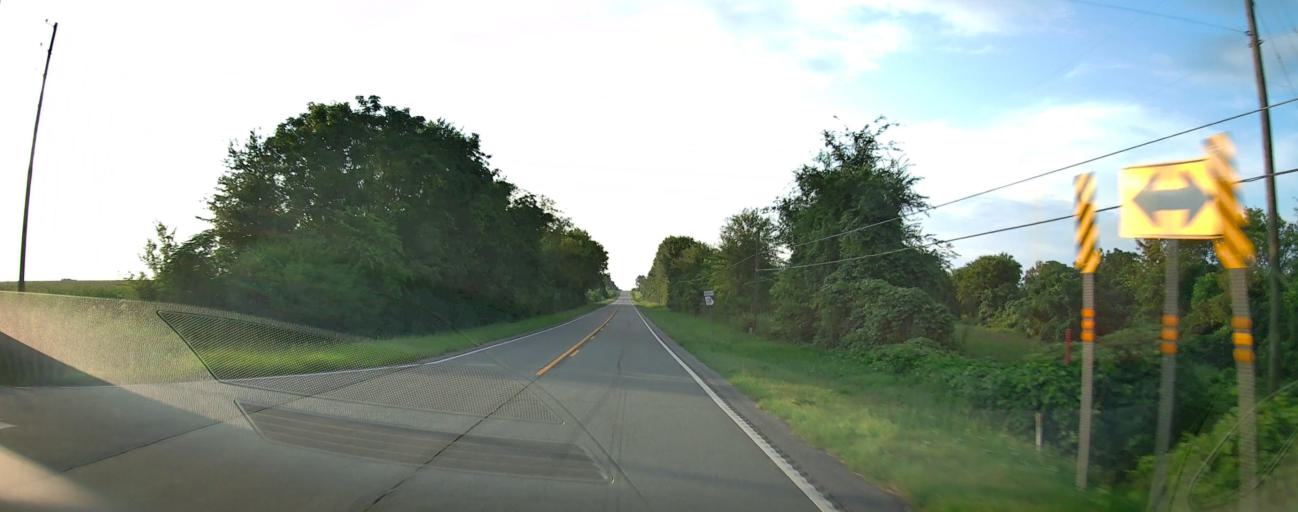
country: US
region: Georgia
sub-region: Taylor County
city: Reynolds
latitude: 32.5888
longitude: -84.0900
